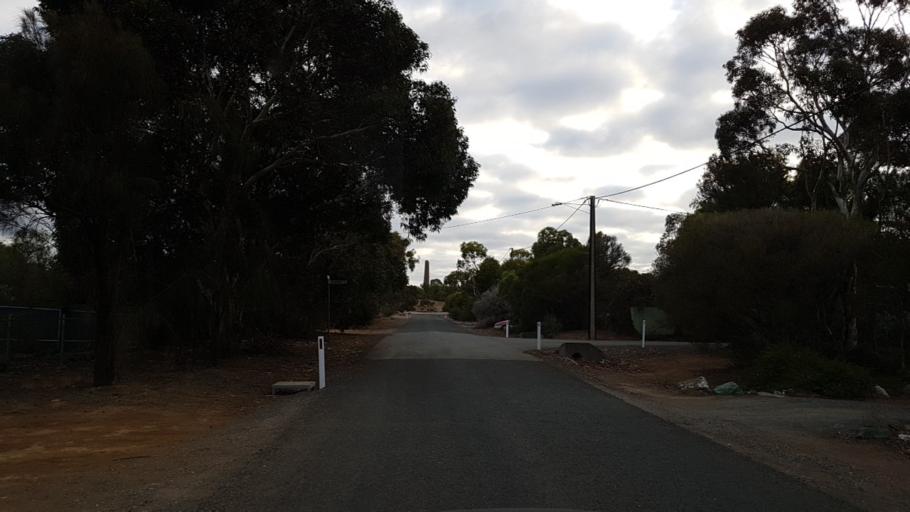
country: AU
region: South Australia
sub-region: Mount Barker
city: Callington
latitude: -35.1150
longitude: 139.0355
